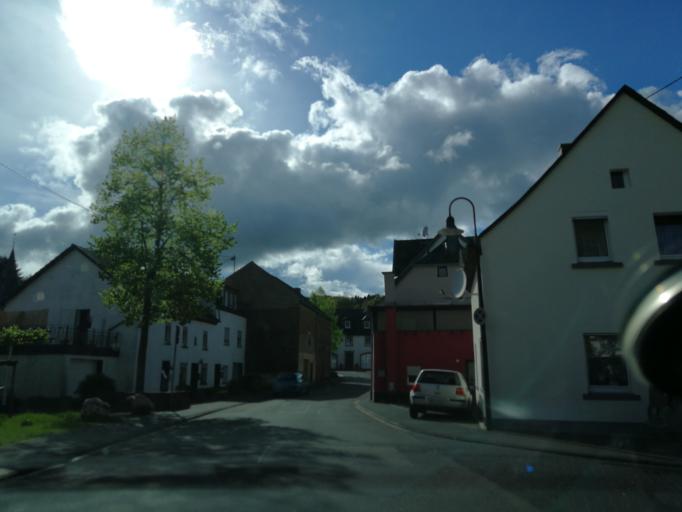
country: DE
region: Rheinland-Pfalz
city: Wittlich
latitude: 50.0014
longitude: 6.9053
